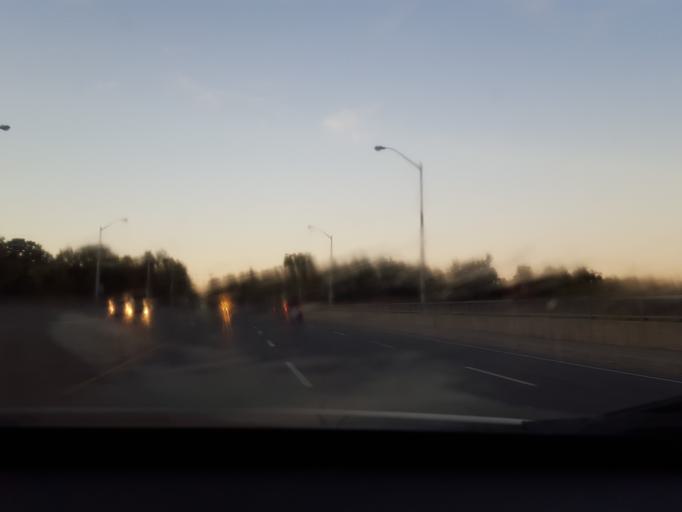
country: CA
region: Ontario
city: Willowdale
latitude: 43.7293
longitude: -79.3815
